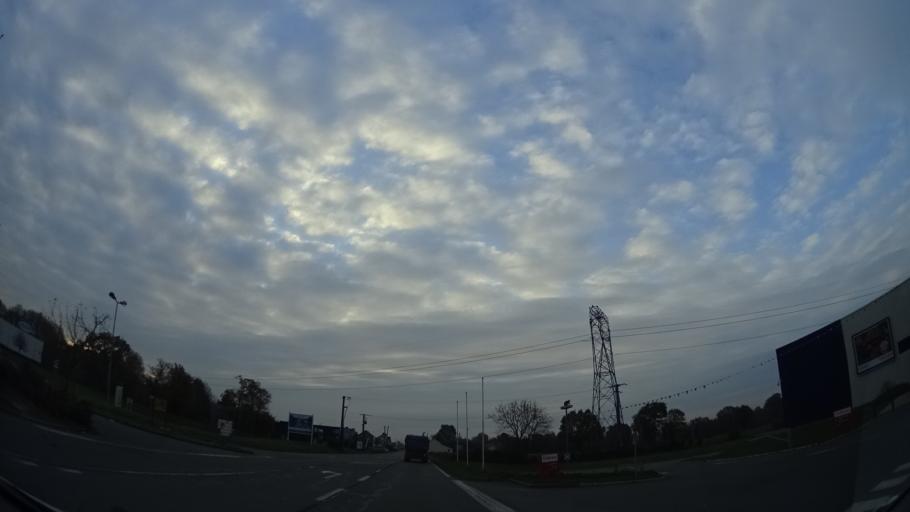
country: FR
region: Brittany
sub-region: Departement d'Ille-et-Vilaine
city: La Chapelle-des-Fougeretz
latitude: 48.1896
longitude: -1.7279
